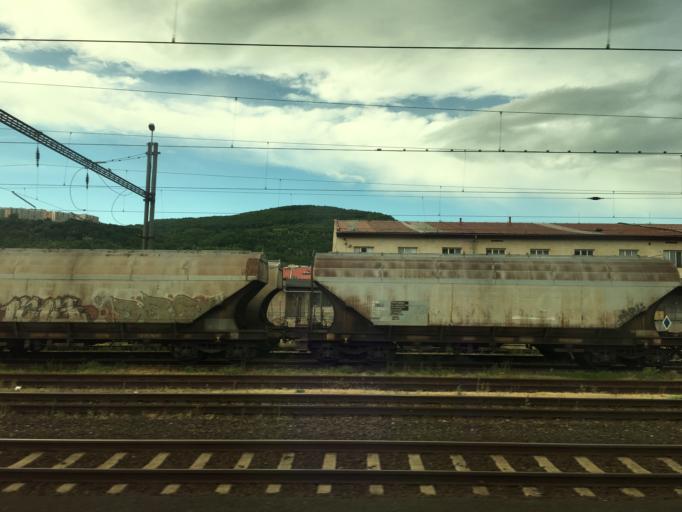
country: CZ
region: Ustecky
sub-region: Okres Usti nad Labem
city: Usti nad Labem
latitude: 50.6639
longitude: 14.0686
